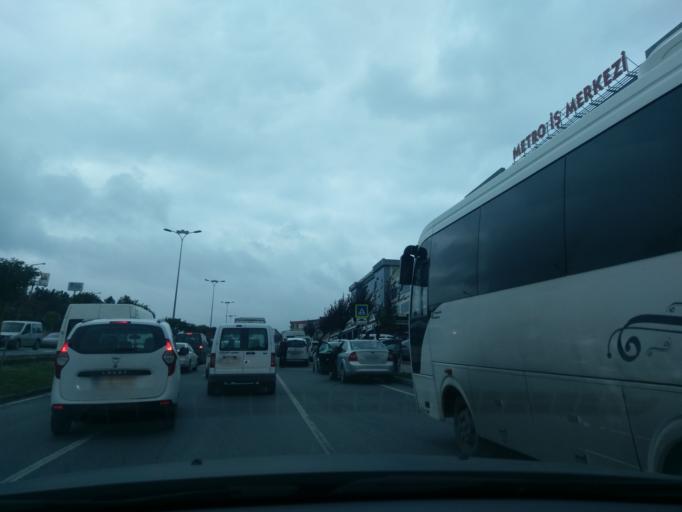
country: TR
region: Istanbul
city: Basaksehir
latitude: 41.0759
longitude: 28.7991
